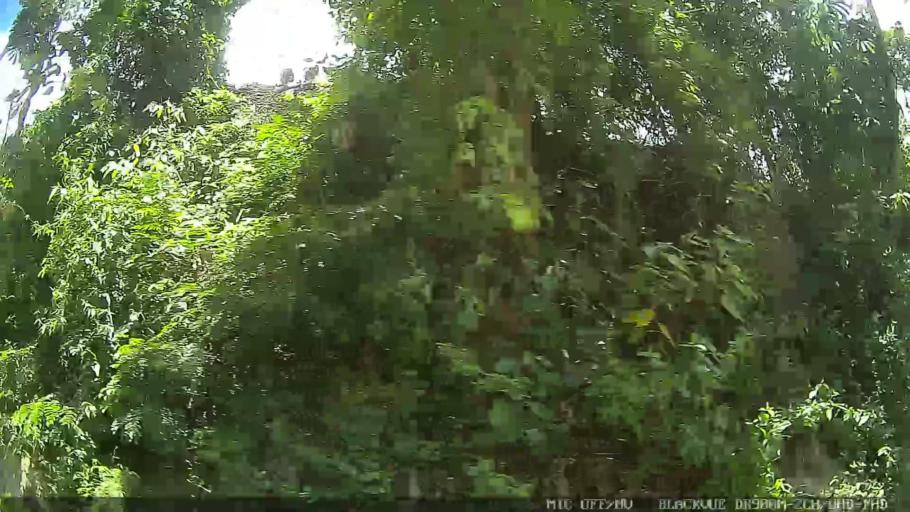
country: BR
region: Sao Paulo
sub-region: Serra Negra
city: Serra Negra
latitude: -22.5892
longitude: -46.7091
